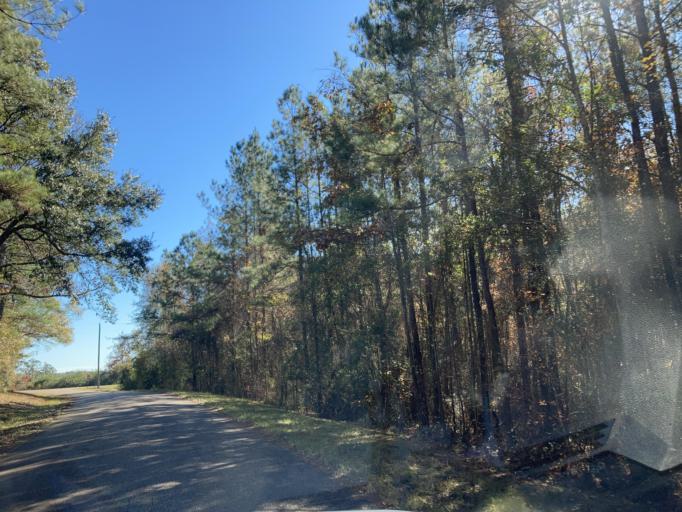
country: US
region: Mississippi
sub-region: Lamar County
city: Sumrall
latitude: 31.3094
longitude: -89.6072
